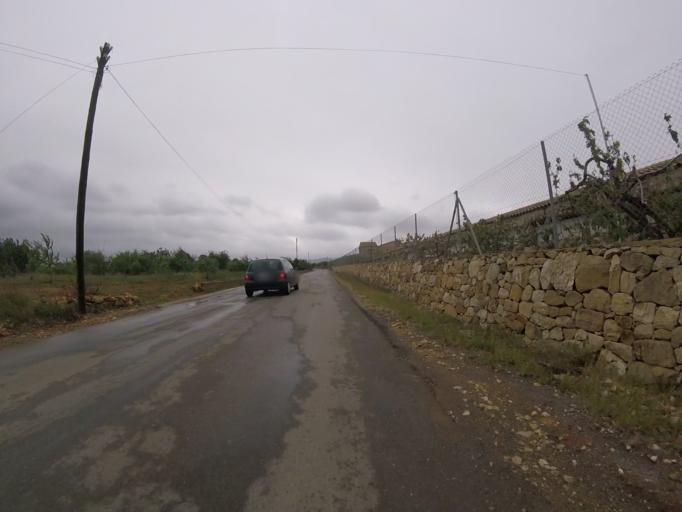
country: ES
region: Valencia
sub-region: Provincia de Castello
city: Alcoceber
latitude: 40.2407
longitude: 0.2492
